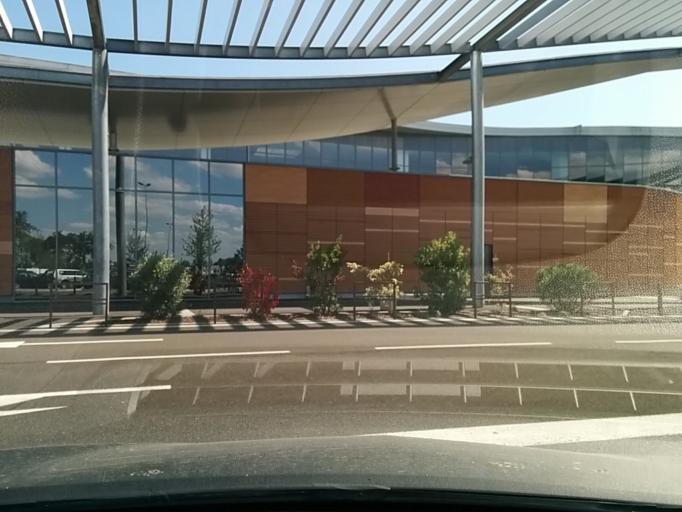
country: FR
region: Aquitaine
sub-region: Departement des Landes
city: Mont-de-Marsan
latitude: 43.8646
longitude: -0.4812
